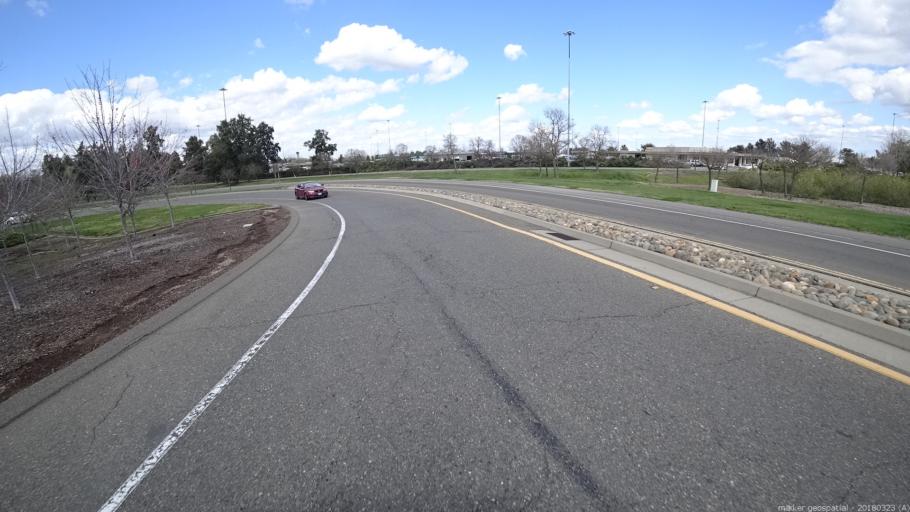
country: US
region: California
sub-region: Yolo County
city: West Sacramento
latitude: 38.6794
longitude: -121.5894
